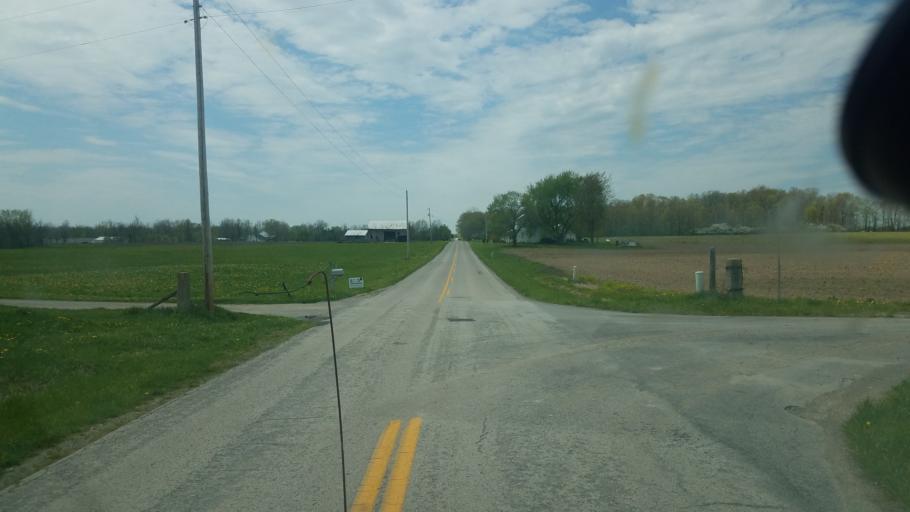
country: US
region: Ohio
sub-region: Hardin County
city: Ada
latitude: 40.7925
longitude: -83.9178
